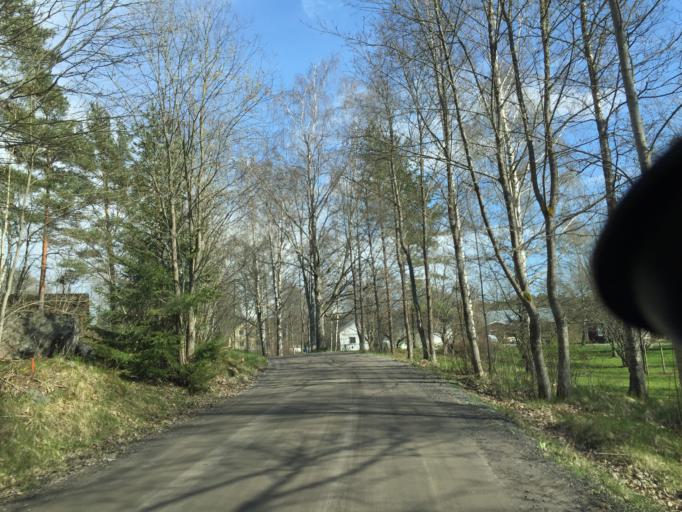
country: FI
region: Uusimaa
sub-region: Raaseporin
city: Hanko
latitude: 59.9429
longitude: 22.9163
